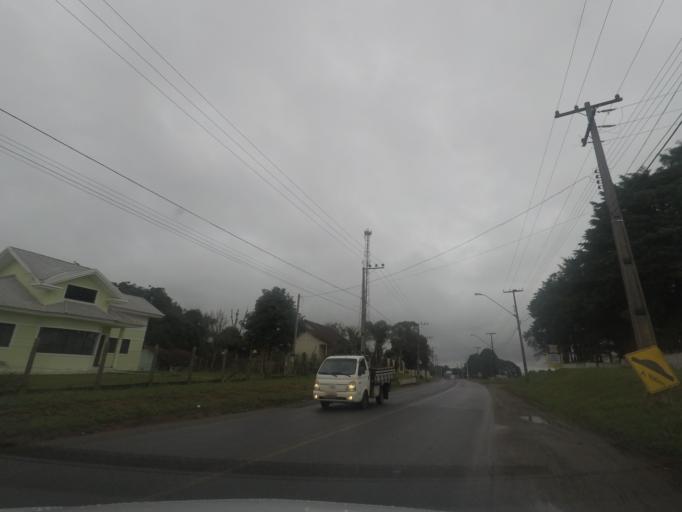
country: BR
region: Parana
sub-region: Quatro Barras
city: Quatro Barras
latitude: -25.3414
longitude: -49.0823
